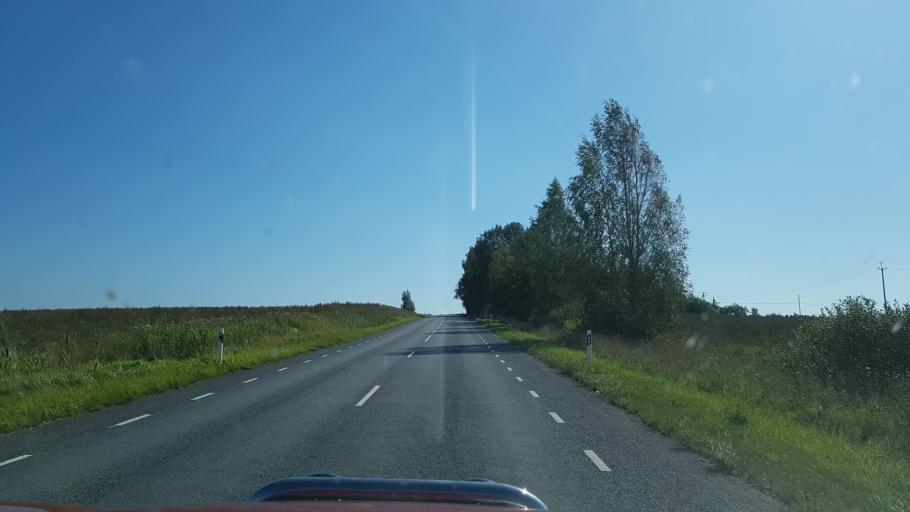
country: EE
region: Polvamaa
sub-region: Polva linn
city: Polva
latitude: 58.2784
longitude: 27.0653
